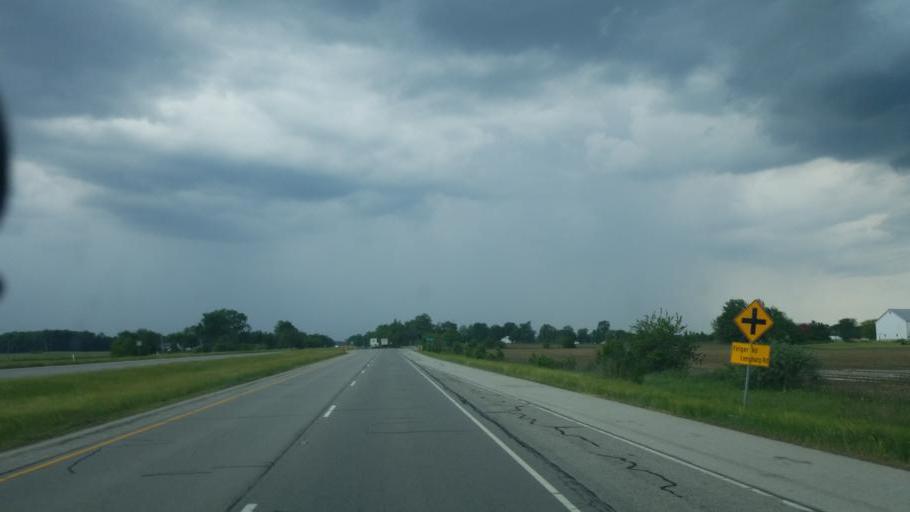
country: US
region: Indiana
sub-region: Whitley County
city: Churubusco
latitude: 41.1259
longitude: -85.2807
